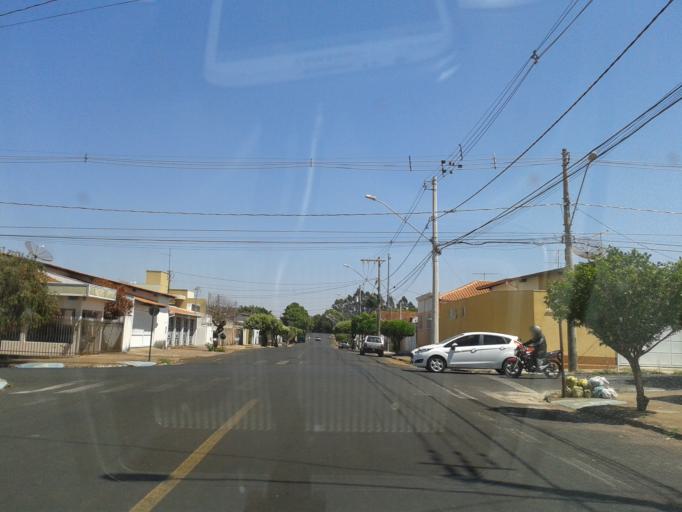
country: BR
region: Minas Gerais
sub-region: Araguari
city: Araguari
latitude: -18.6420
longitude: -48.1934
